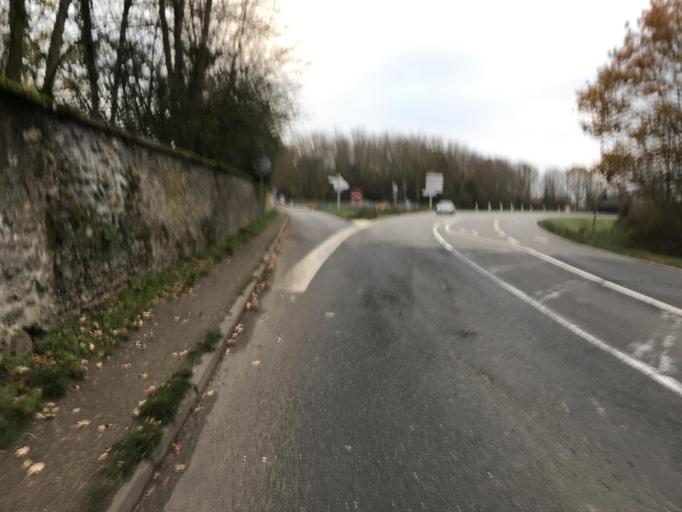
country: FR
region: Ile-de-France
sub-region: Departement des Yvelines
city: Chateaufort
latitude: 48.7345
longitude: 2.0974
